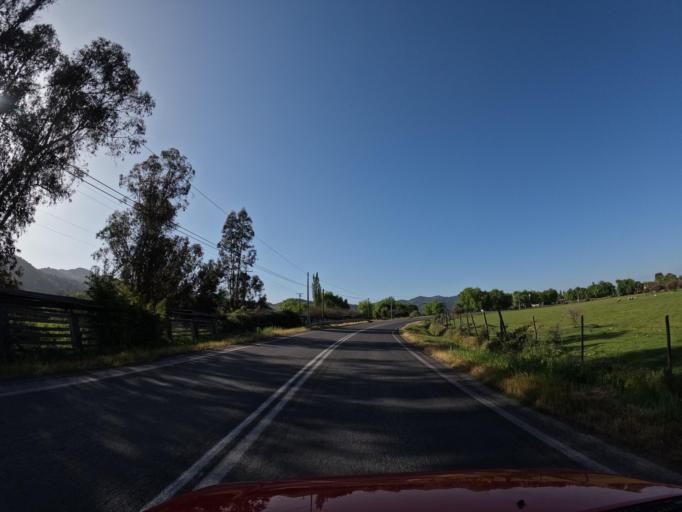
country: CL
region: Maule
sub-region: Provincia de Curico
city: Teno
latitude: -34.8507
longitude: -71.1928
